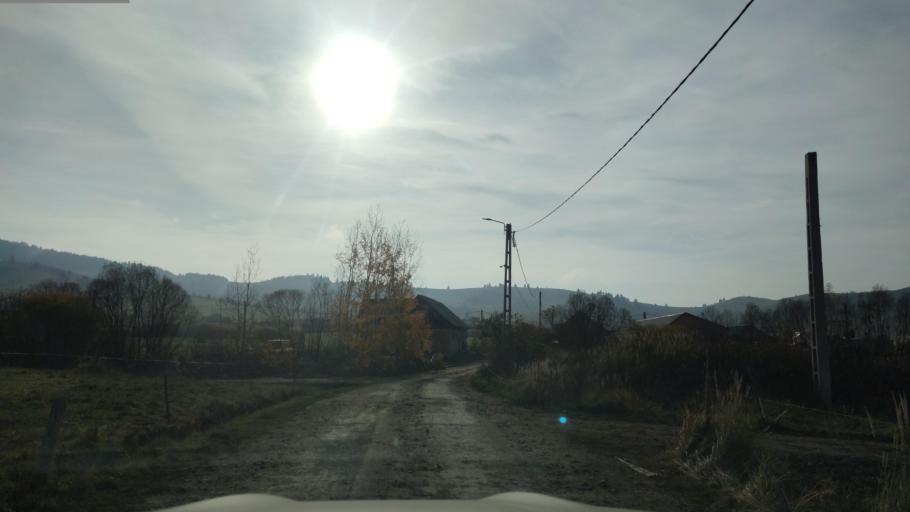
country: RO
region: Harghita
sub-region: Comuna Ditrau
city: Ditrau
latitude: 46.8222
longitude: 25.5363
